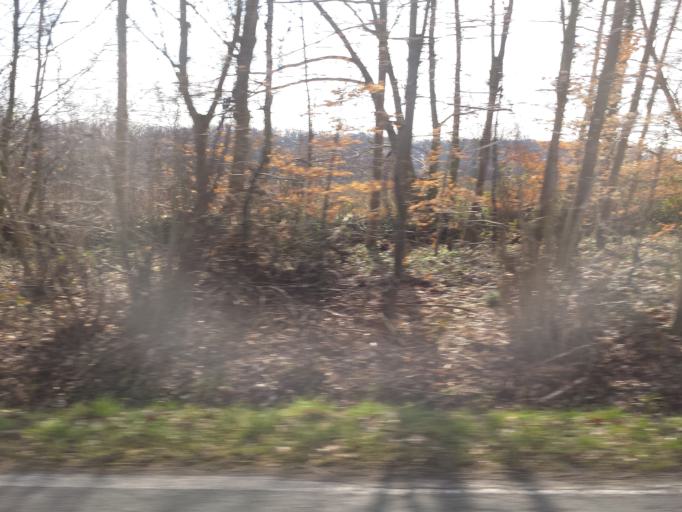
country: DE
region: North Rhine-Westphalia
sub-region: Regierungsbezirk Munster
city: Havixbeck
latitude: 51.9455
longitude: 7.4760
